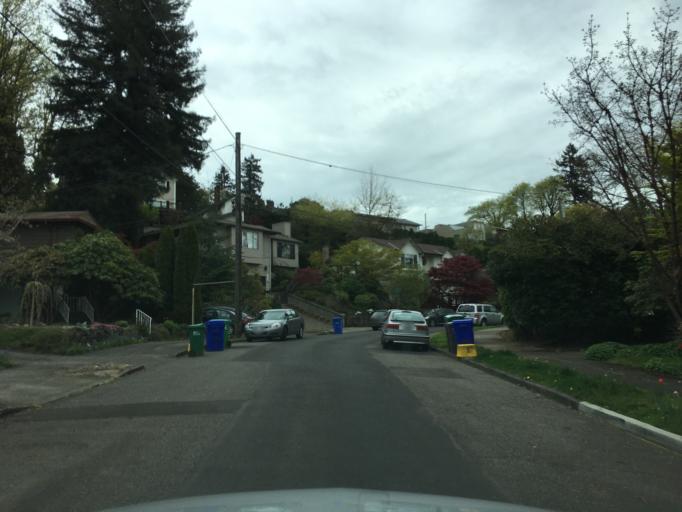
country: US
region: Oregon
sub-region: Multnomah County
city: Lents
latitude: 45.5224
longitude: -122.5965
